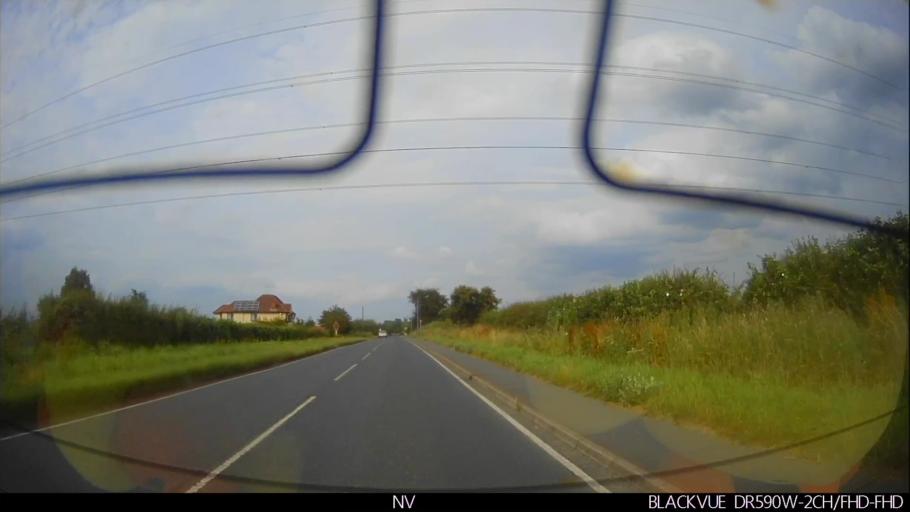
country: GB
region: England
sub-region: City of York
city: Huntington
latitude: 54.0150
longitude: -1.0496
